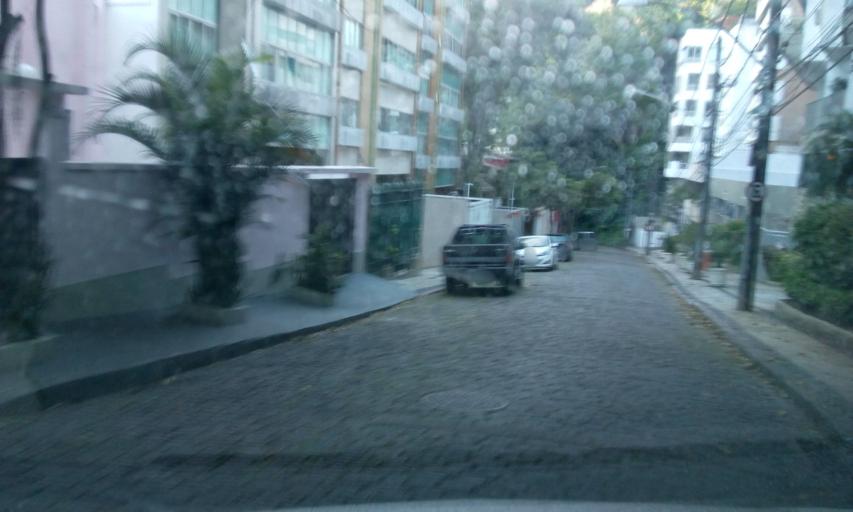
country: BR
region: Rio de Janeiro
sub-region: Rio De Janeiro
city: Rio de Janeiro
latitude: -22.9663
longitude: -43.2000
